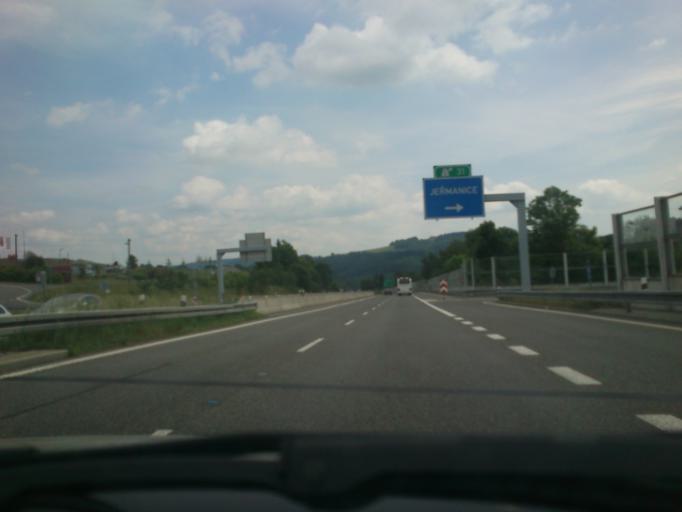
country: CZ
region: Liberecky
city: Hodkovice nad Mohelkou
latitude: 50.7005
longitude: 15.0962
